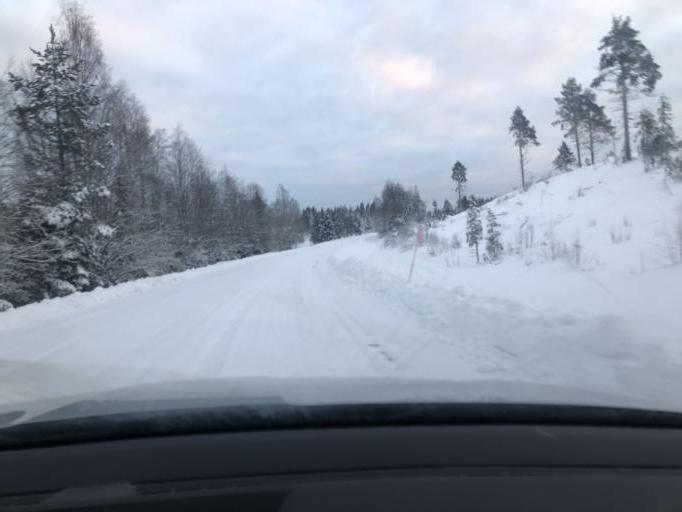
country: SE
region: Vaesternorrland
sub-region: Kramfors Kommun
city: Nordingra
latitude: 62.9943
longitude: 18.2483
